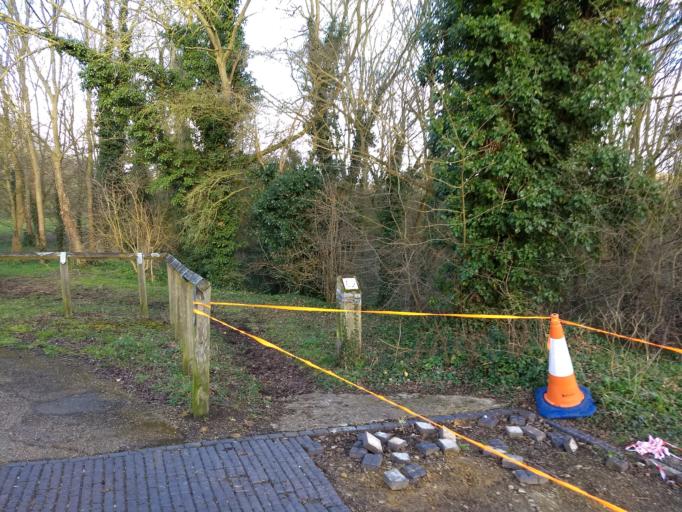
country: GB
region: England
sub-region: Milton Keynes
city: Milton Keynes
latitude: 52.0486
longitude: -0.7334
